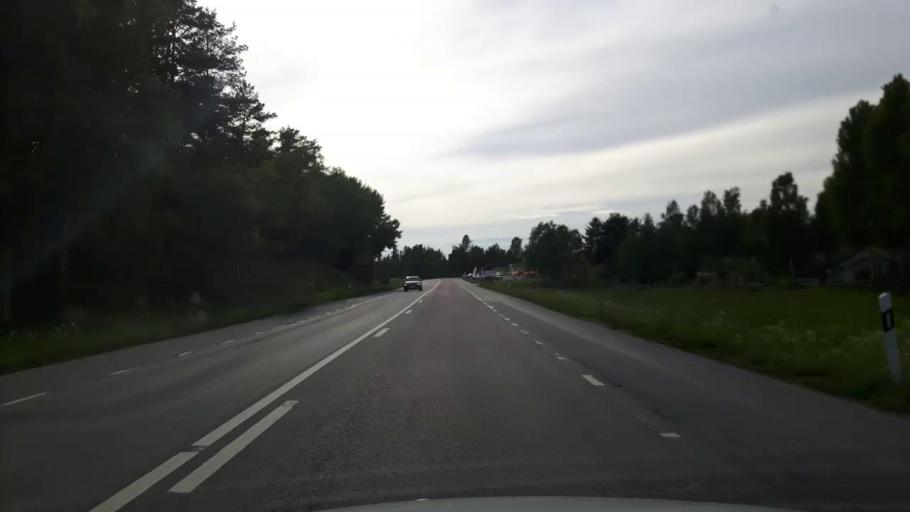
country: SE
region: Uppsala
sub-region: Enkopings Kommun
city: Orsundsbro
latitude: 59.6605
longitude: 17.3265
